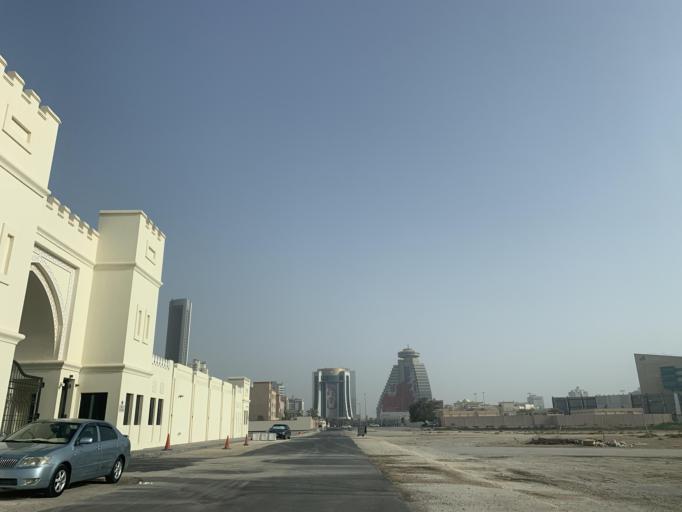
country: BH
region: Manama
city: Jidd Hafs
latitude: 26.2372
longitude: 50.5455
